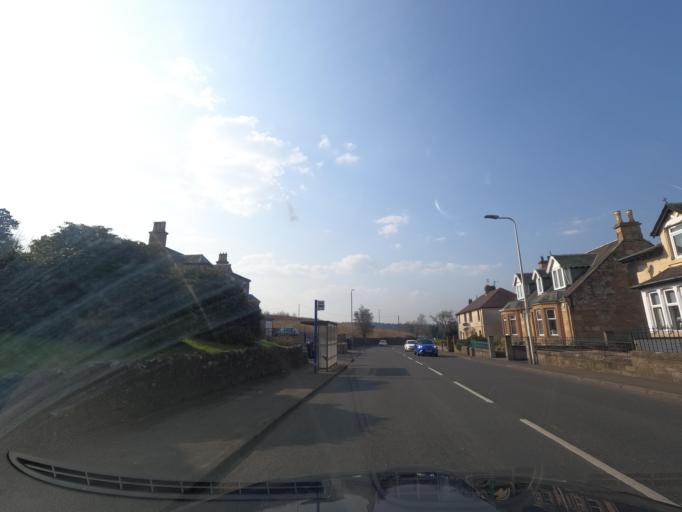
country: GB
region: Scotland
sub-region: Falkirk
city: Grangemouth
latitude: 55.9879
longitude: -3.7410
